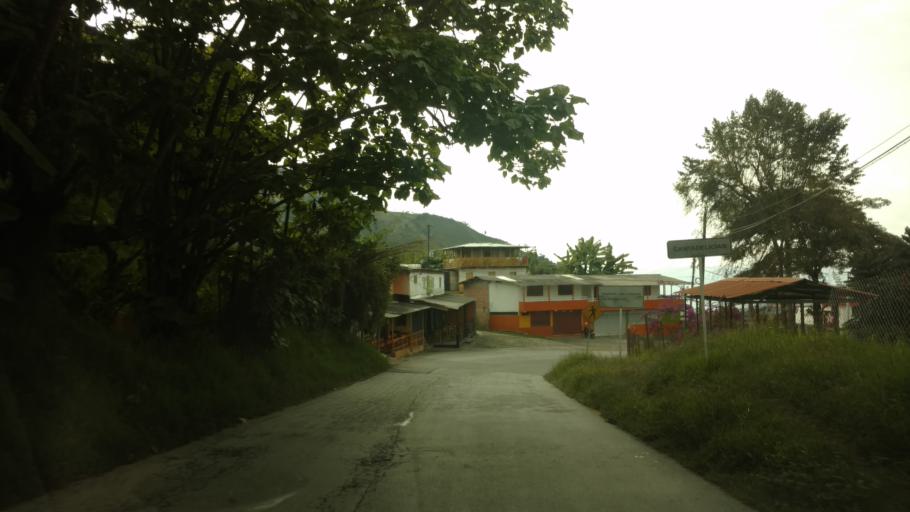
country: CO
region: Caldas
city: Neira
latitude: 5.1747
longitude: -75.5217
